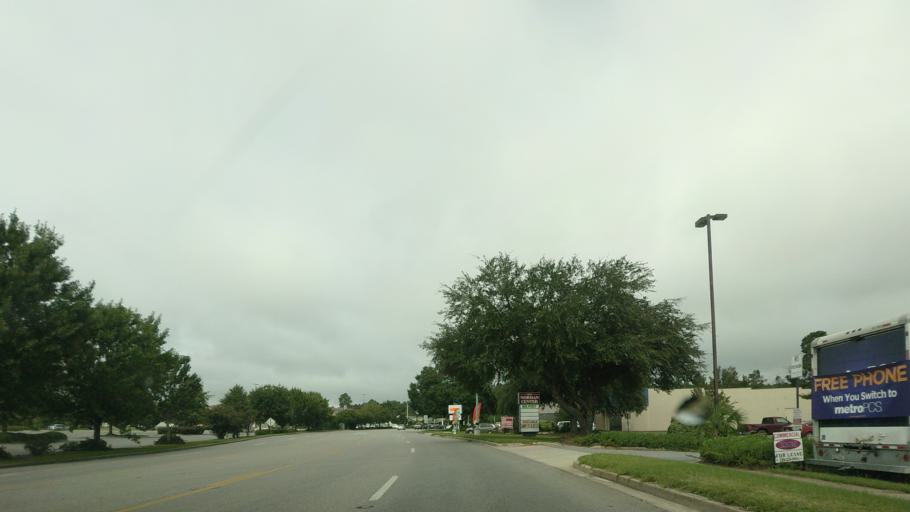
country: US
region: Georgia
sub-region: Lowndes County
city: Remerton
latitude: 30.8453
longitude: -83.3180
